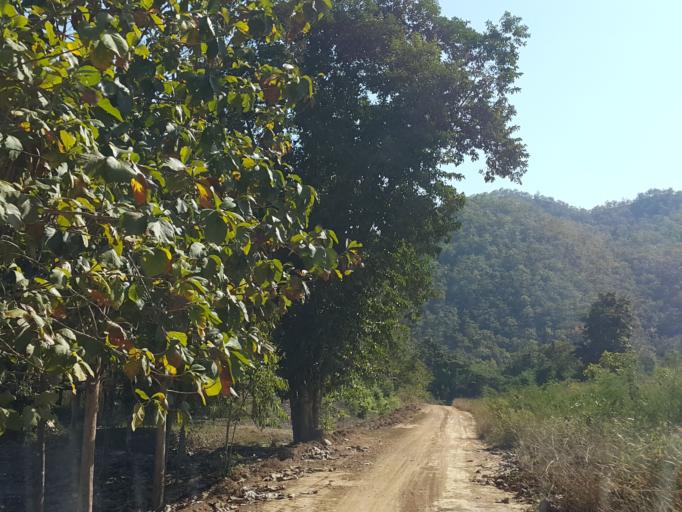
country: TH
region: Sukhothai
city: Thung Saliam
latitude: 17.3219
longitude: 99.4613
